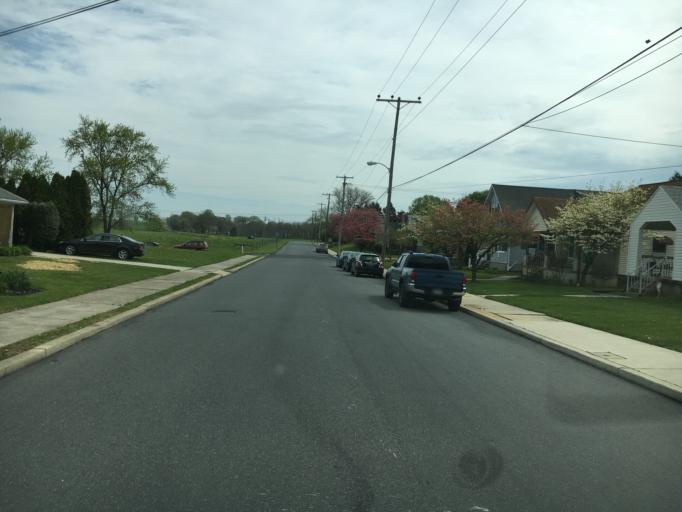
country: US
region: Pennsylvania
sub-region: Berks County
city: Fleetwood
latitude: 40.4591
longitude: -75.8143
